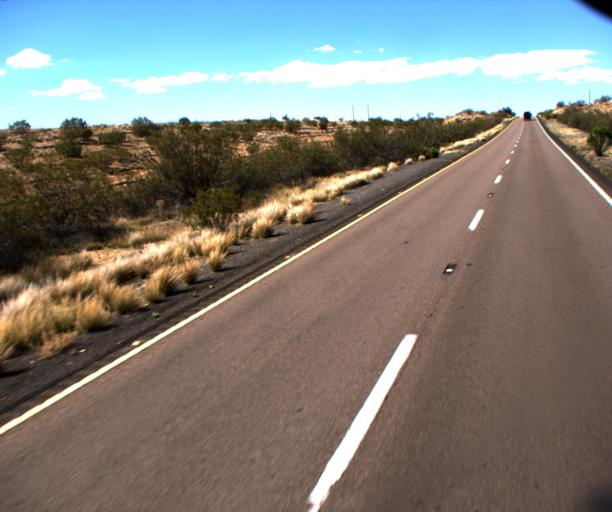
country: US
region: Arizona
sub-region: Mohave County
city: Kingman
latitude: 35.0236
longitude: -113.6641
